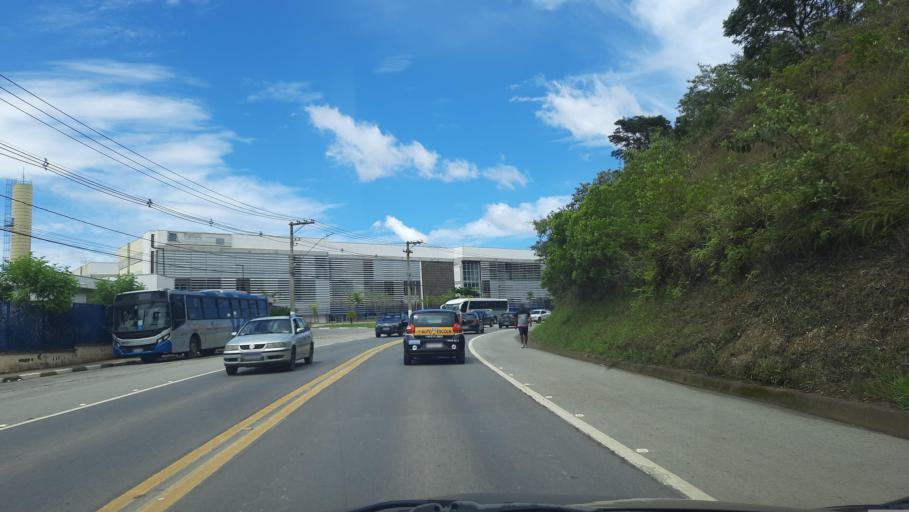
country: BR
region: Sao Paulo
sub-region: Franco Da Rocha
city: Franco da Rocha
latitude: -23.3353
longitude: -46.7212
